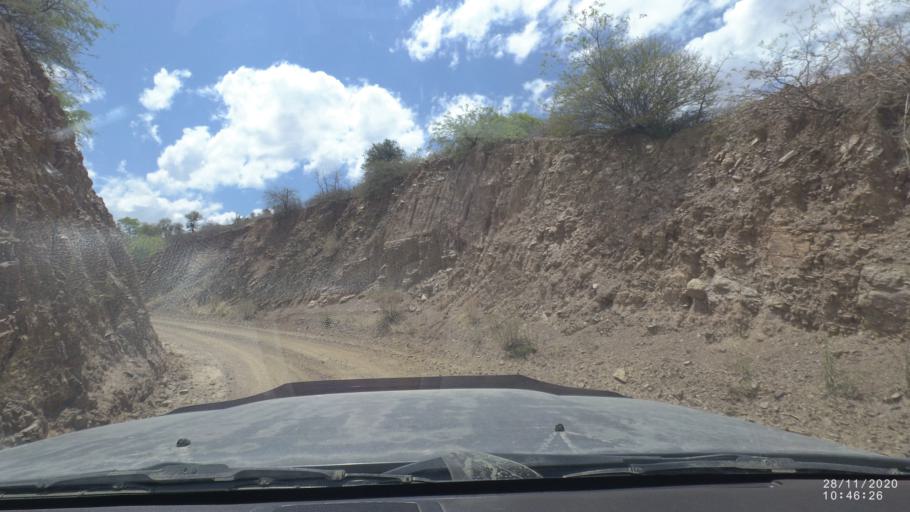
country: BO
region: Cochabamba
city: Capinota
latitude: -17.7879
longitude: -66.1293
